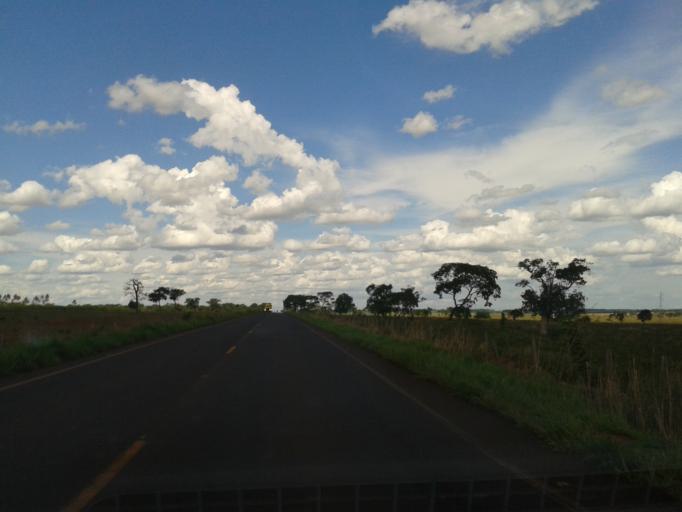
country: BR
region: Minas Gerais
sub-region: Iturama
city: Iturama
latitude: -19.6947
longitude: -50.1613
